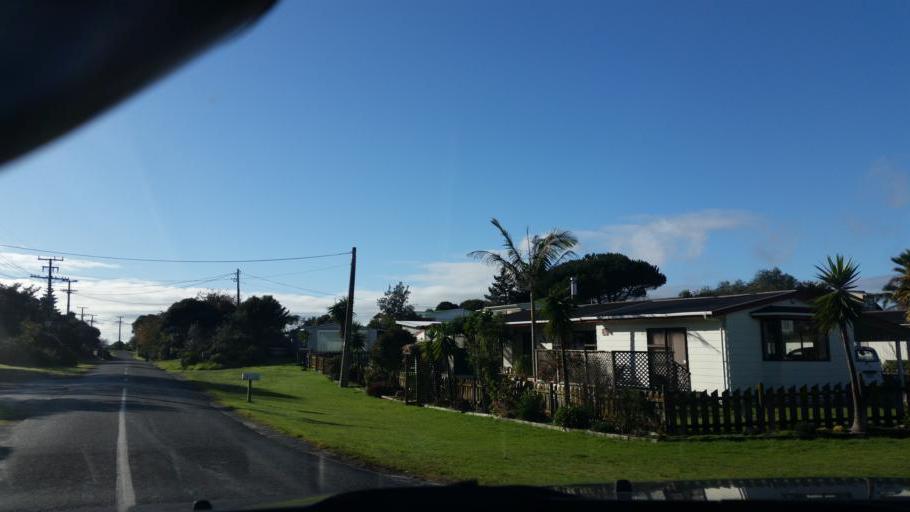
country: NZ
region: Auckland
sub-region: Auckland
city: Wellsford
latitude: -36.0882
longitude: 174.5851
